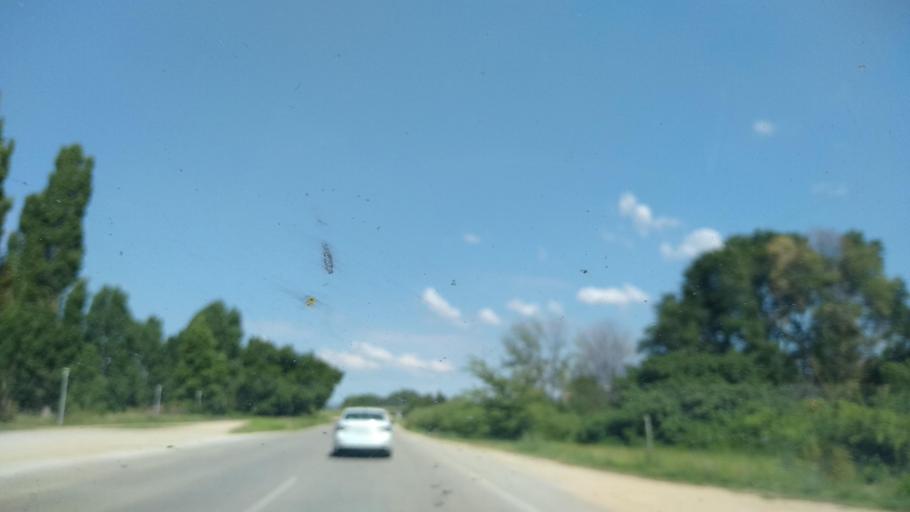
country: GR
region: Central Macedonia
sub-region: Nomos Thessalonikis
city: Nea Apollonia
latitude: 40.6345
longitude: 23.5044
